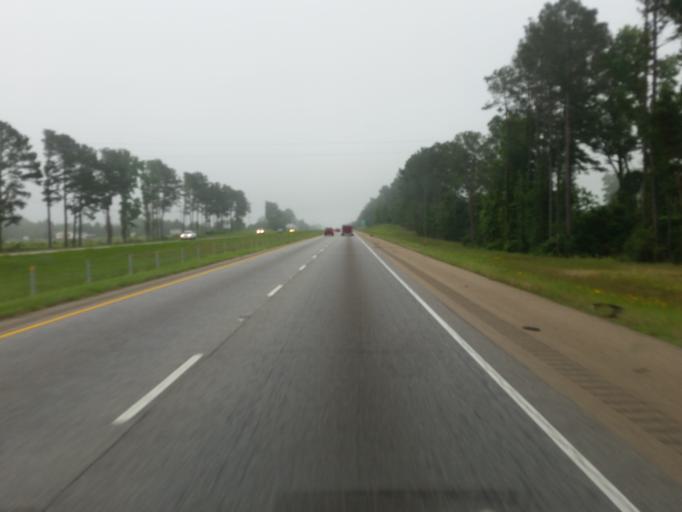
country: US
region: Louisiana
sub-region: Webster Parish
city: Minden
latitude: 32.5856
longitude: -93.2726
